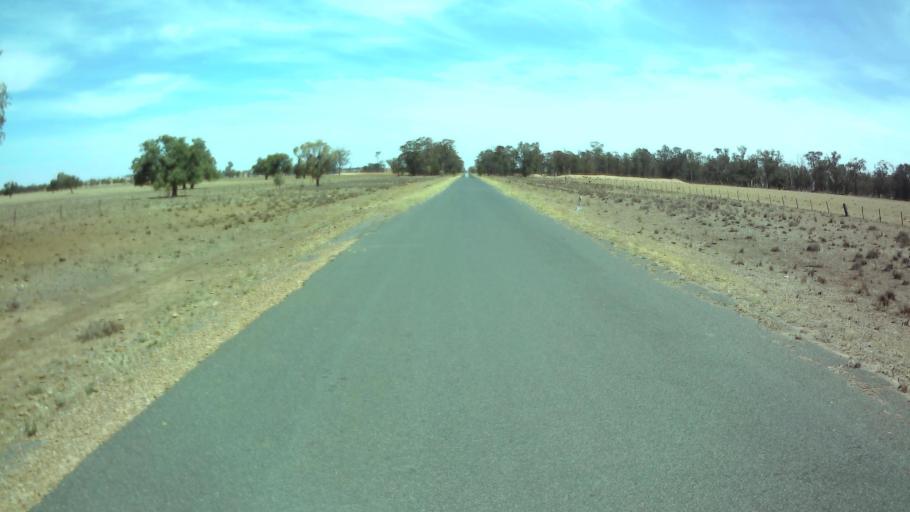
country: AU
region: New South Wales
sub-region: Weddin
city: Grenfell
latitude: -33.8607
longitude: 147.7466
